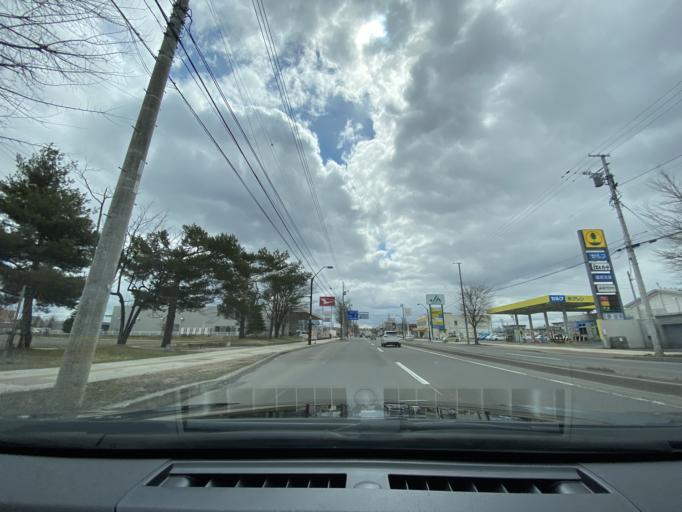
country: JP
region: Hokkaido
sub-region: Asahikawa-shi
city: Asahikawa
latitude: 43.7568
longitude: 142.3506
